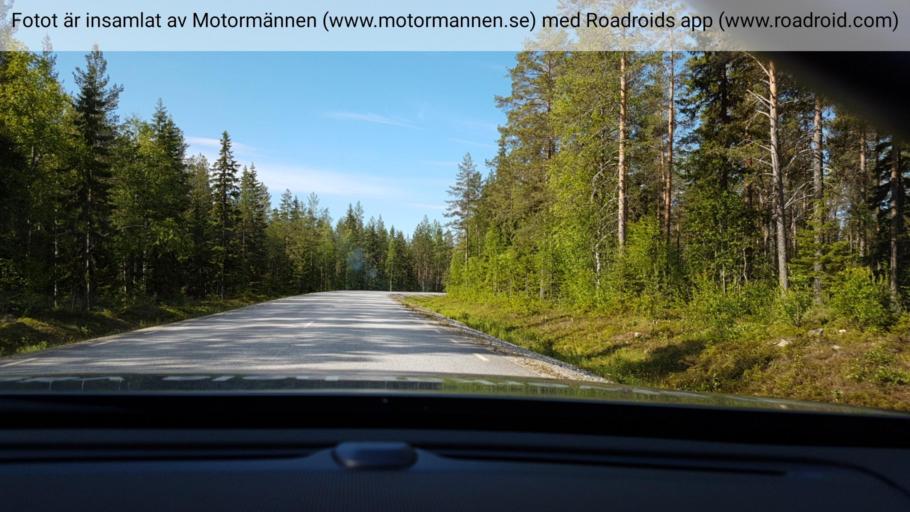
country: SE
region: Vaesterbotten
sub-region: Bjurholms Kommun
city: Bjurholm
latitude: 64.1741
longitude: 19.3993
